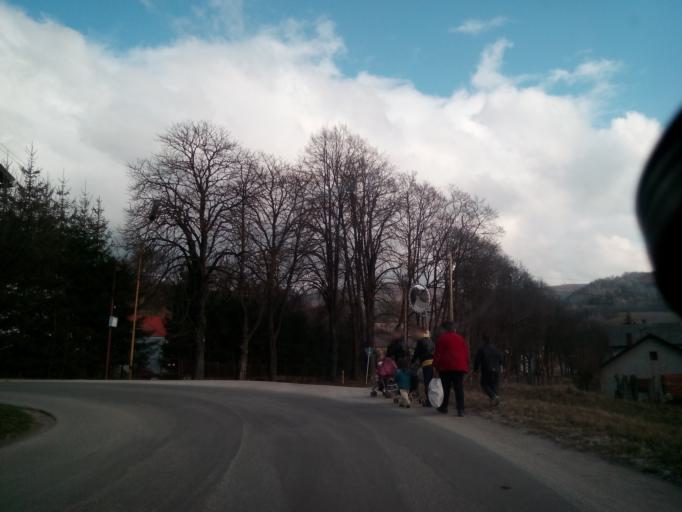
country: SK
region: Kosicky
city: Dobsina
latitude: 48.7187
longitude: 20.2685
